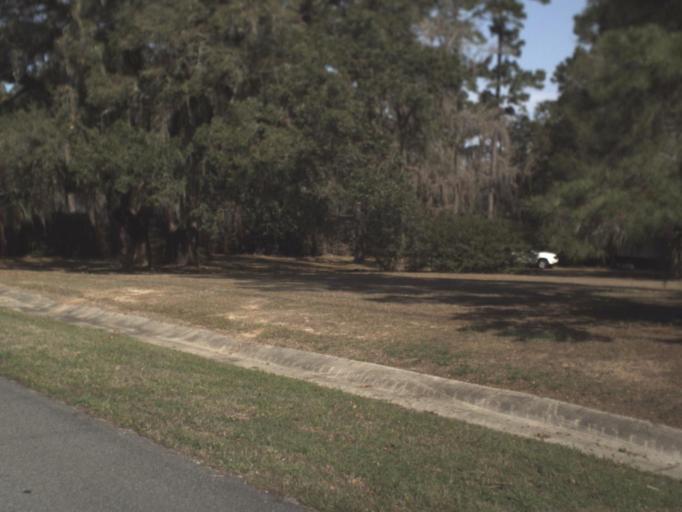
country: US
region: Florida
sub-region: Leon County
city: Tallahassee
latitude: 30.5093
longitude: -84.3394
